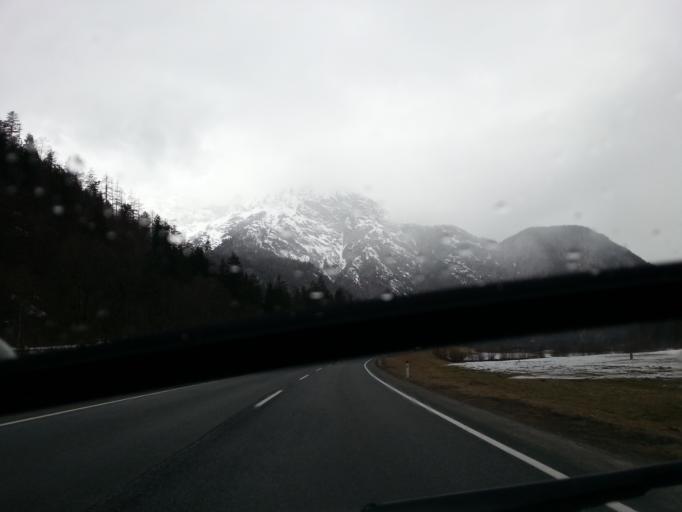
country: AT
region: Salzburg
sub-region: Politischer Bezirk Zell am See
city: Sankt Martin bei Lofer
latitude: 47.5270
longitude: 12.7386
